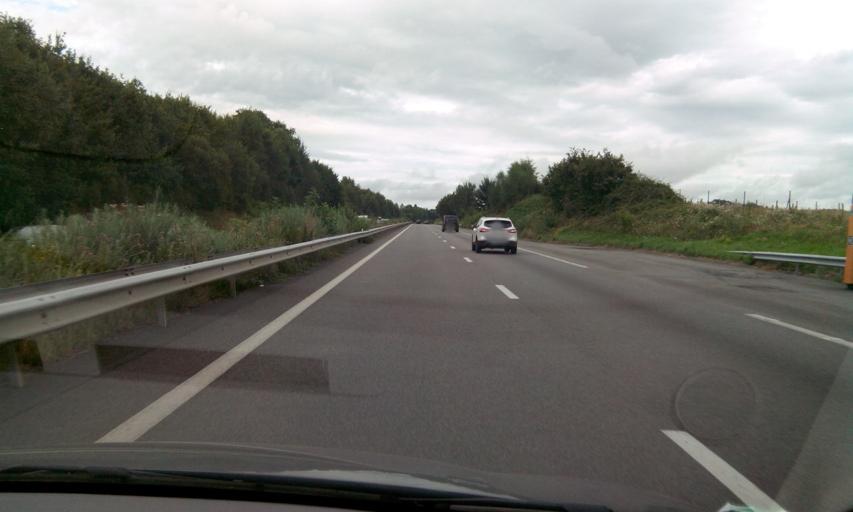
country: FR
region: Limousin
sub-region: Departement de la Correze
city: Uzerche
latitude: 45.4450
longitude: 1.5099
